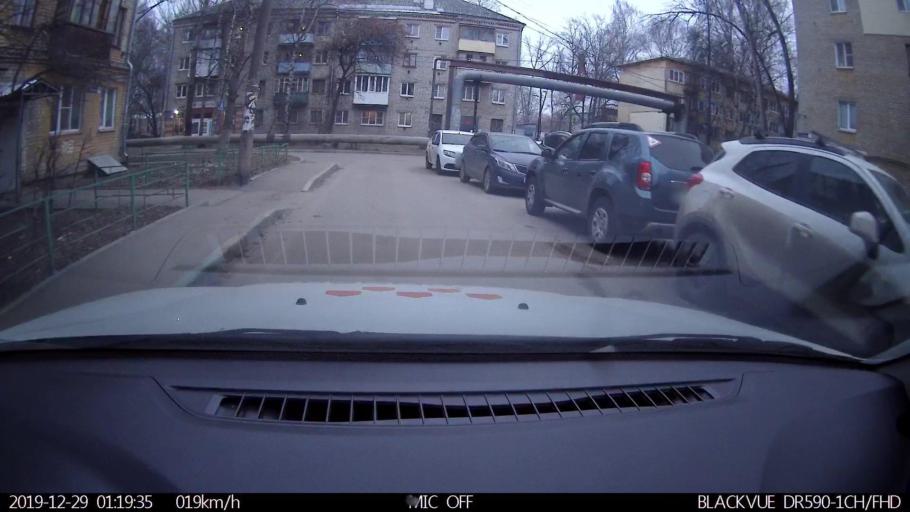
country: RU
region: Nizjnij Novgorod
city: Nizhniy Novgorod
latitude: 56.2753
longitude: 43.9251
